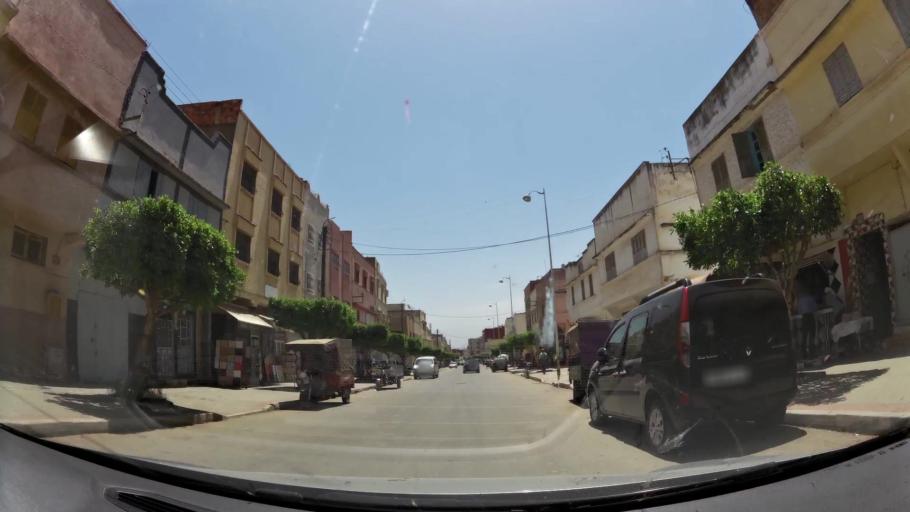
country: MA
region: Rabat-Sale-Zemmour-Zaer
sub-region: Khemisset
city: Khemisset
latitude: 33.8319
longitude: -6.0749
